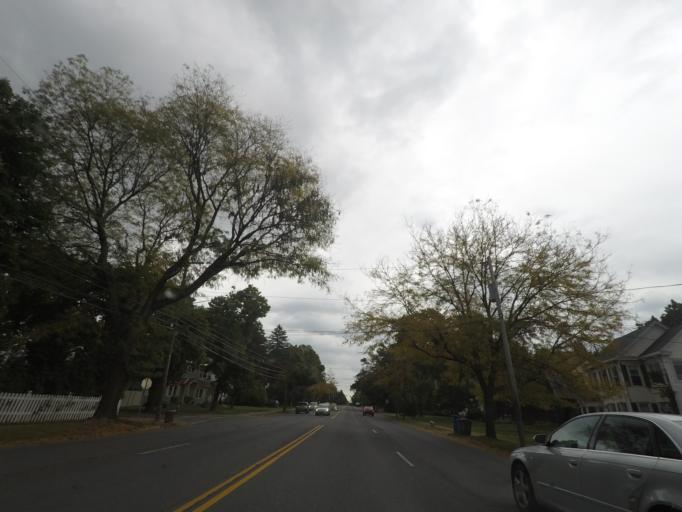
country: US
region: New York
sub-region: Albany County
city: West Albany
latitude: 42.6684
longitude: -73.7979
